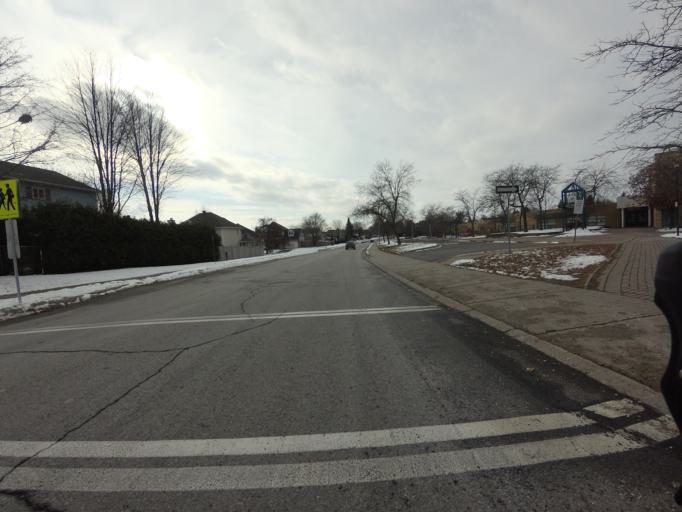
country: CA
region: Ontario
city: Bells Corners
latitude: 45.2687
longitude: -75.7662
